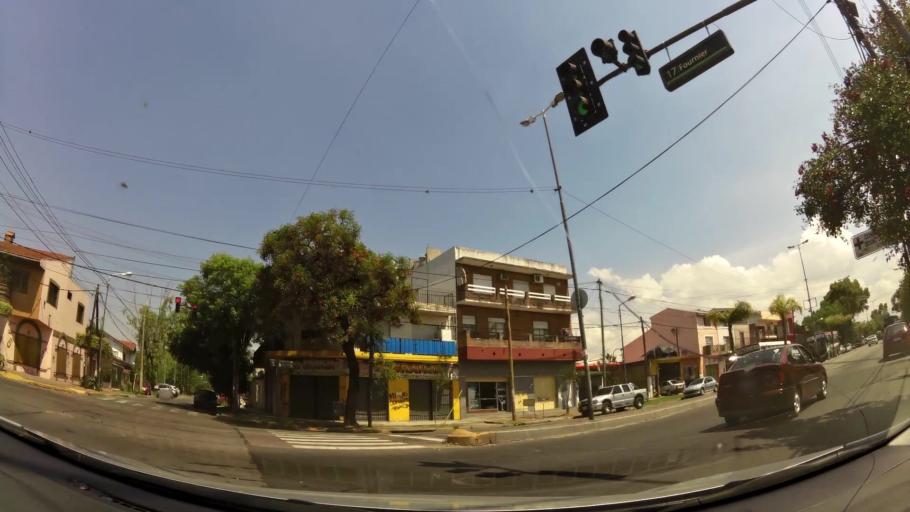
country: AR
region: Buenos Aires
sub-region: Partido de Tigre
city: Tigre
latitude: -34.4648
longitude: -58.5815
